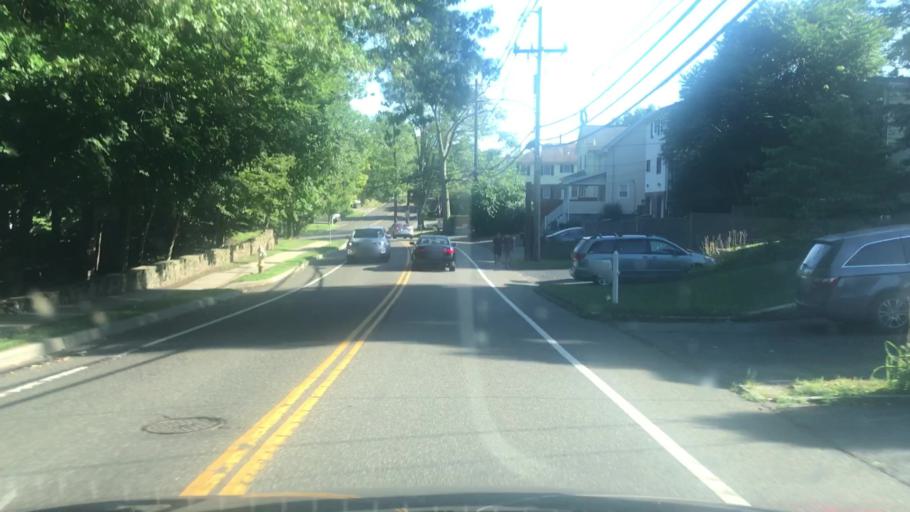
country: US
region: Connecticut
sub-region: Fairfield County
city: Pemberwick
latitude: 41.0183
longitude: -73.6501
